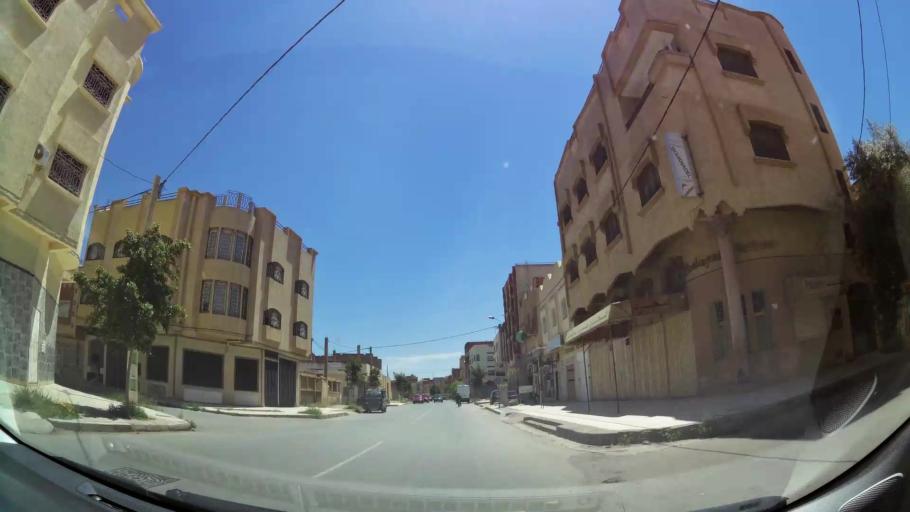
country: MA
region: Oriental
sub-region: Oujda-Angad
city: Oujda
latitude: 34.6723
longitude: -1.8891
